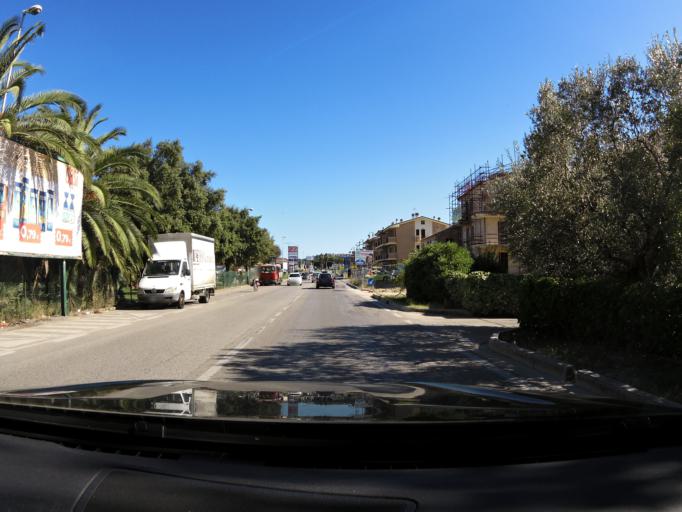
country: IT
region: The Marches
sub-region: Province of Fermo
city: Porto San Giorgio
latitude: 43.1660
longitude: 13.8000
